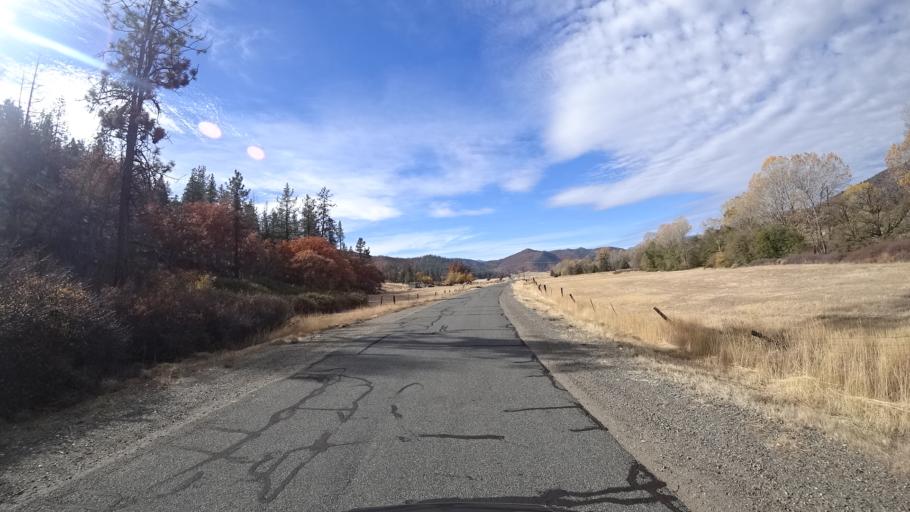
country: US
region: California
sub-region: Siskiyou County
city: Yreka
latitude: 41.6335
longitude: -122.7495
